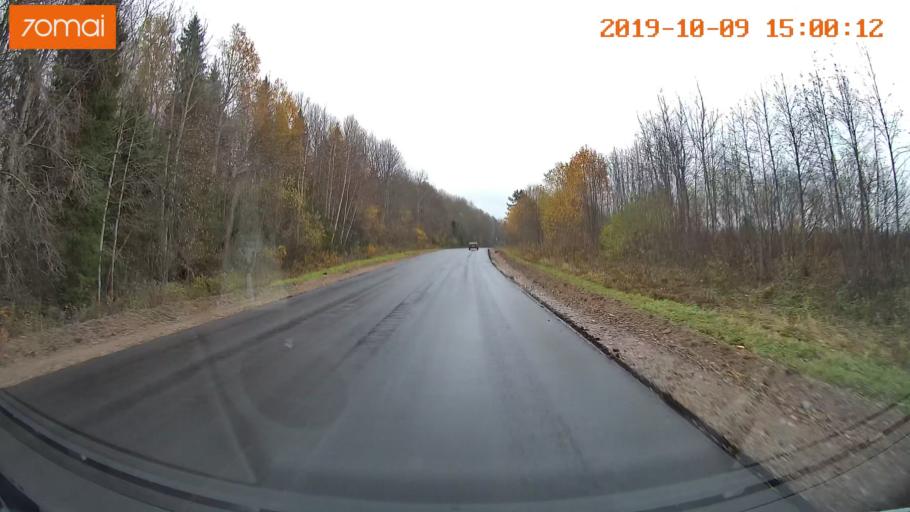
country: RU
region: Kostroma
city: Chistyye Bory
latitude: 58.3120
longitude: 41.6764
